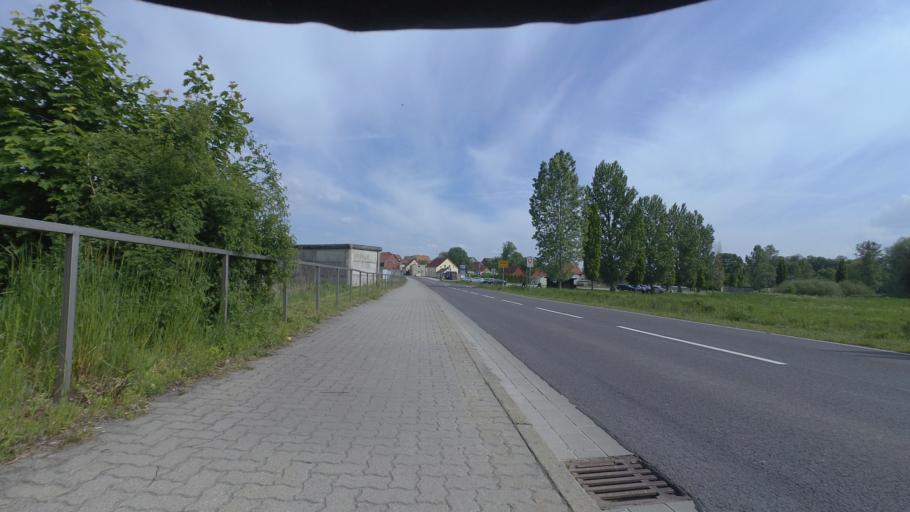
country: DE
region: Saxony-Anhalt
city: Hotensleben
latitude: 52.1228
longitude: 11.0121
